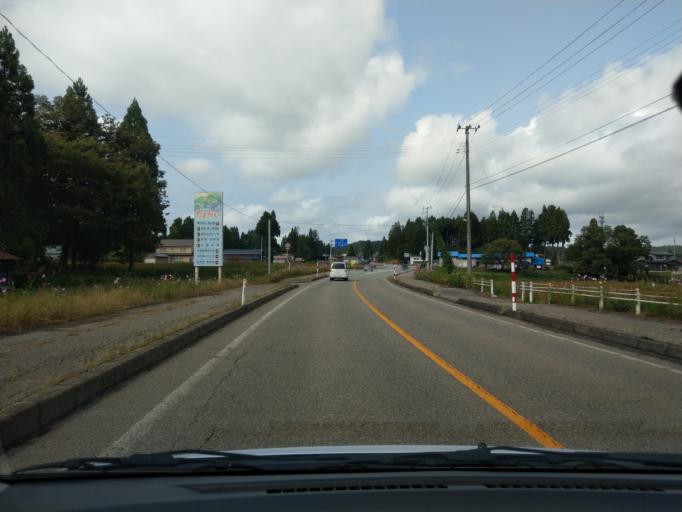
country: JP
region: Akita
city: Omagari
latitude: 39.4374
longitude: 140.3635
